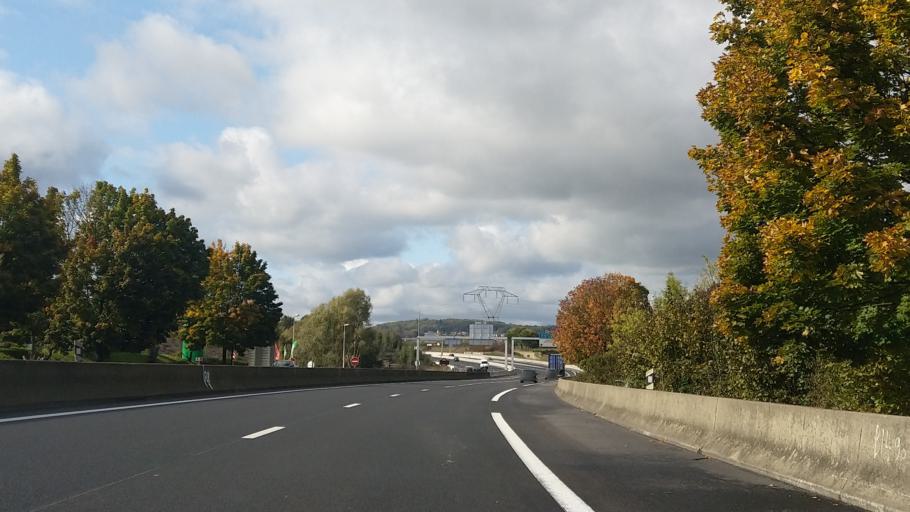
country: FR
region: Ile-de-France
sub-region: Departement du Val-d'Oise
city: Attainville
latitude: 49.0601
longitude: 2.3491
